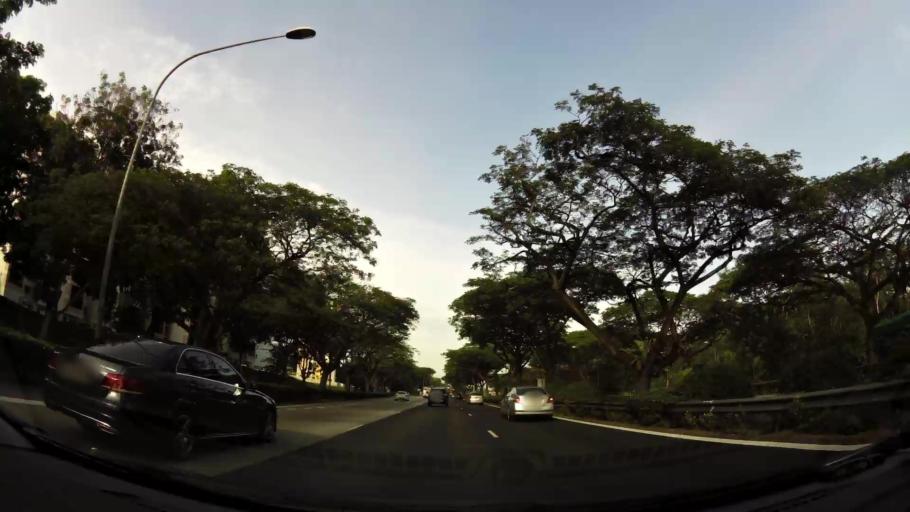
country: MY
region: Johor
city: Johor Bahru
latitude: 1.3554
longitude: 103.7221
